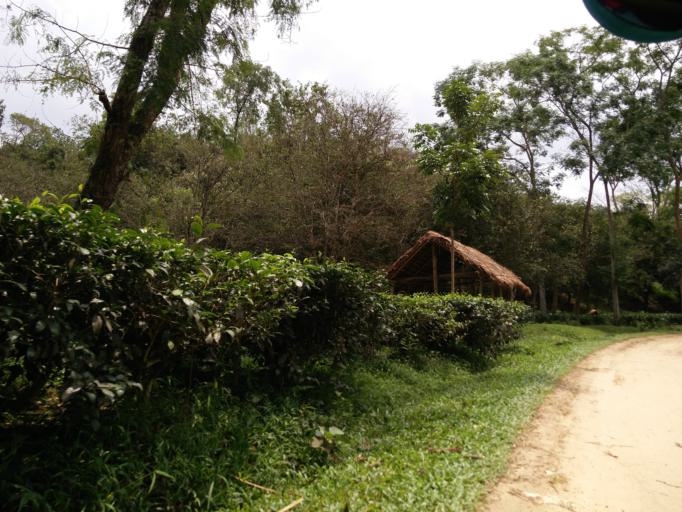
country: IN
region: Tripura
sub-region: Dhalai
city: Kamalpur
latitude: 24.3029
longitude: 91.7926
